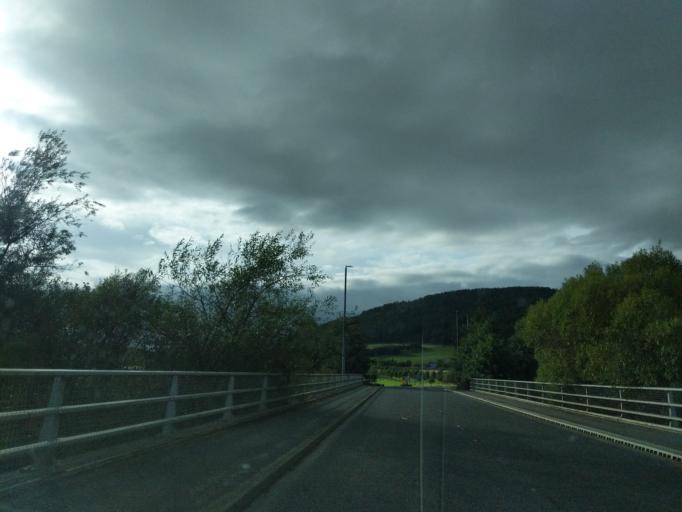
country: GB
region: Scotland
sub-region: The Scottish Borders
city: Innerleithen
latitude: 55.6406
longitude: -3.1147
